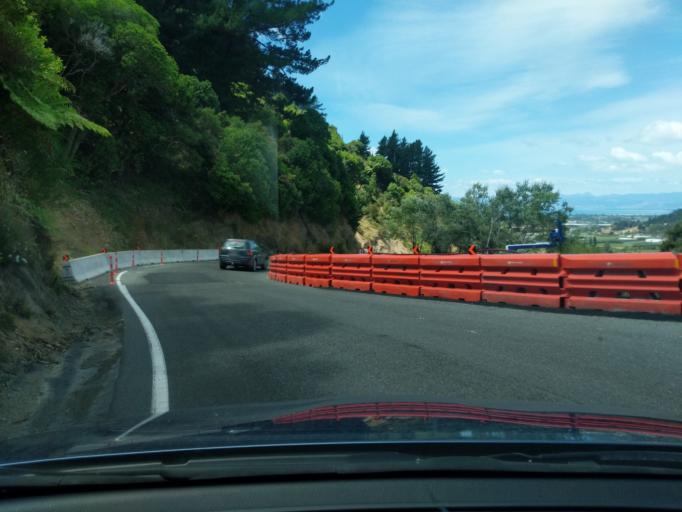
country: NZ
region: Tasman
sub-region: Tasman District
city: Motueka
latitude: -41.0470
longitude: 172.9563
